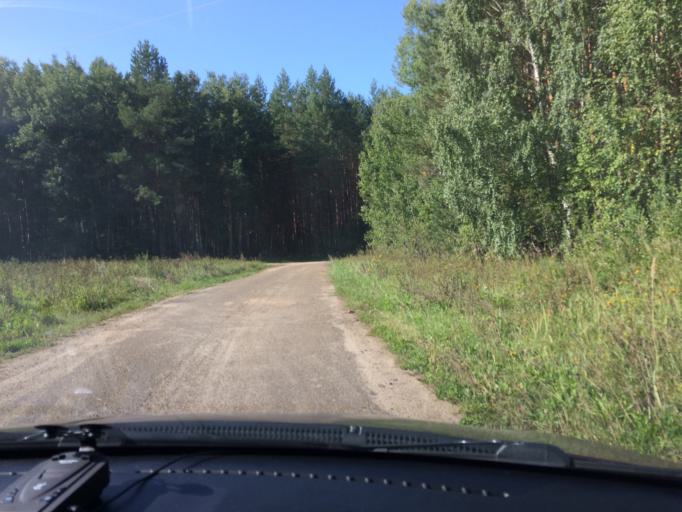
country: RU
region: Mariy-El
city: Sovetskiy
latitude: 56.5757
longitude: 48.4301
